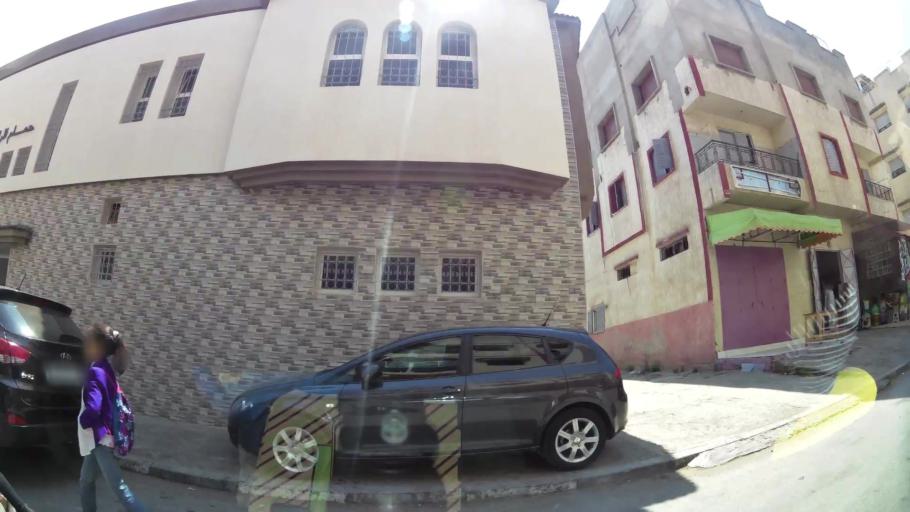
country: MA
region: Rabat-Sale-Zemmour-Zaer
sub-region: Skhirate-Temara
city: Temara
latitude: 33.9692
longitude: -6.8967
